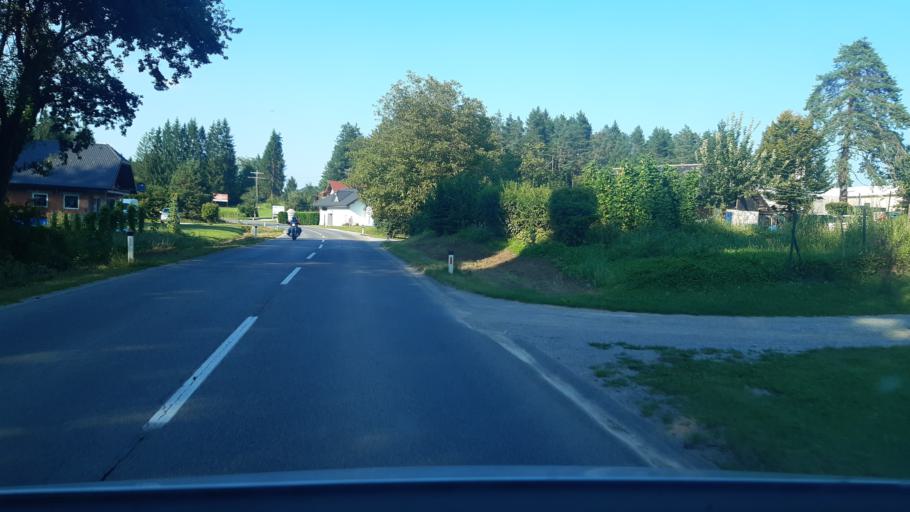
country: SI
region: Crnomelj
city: Crnomelj
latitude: 45.5540
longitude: 15.1653
